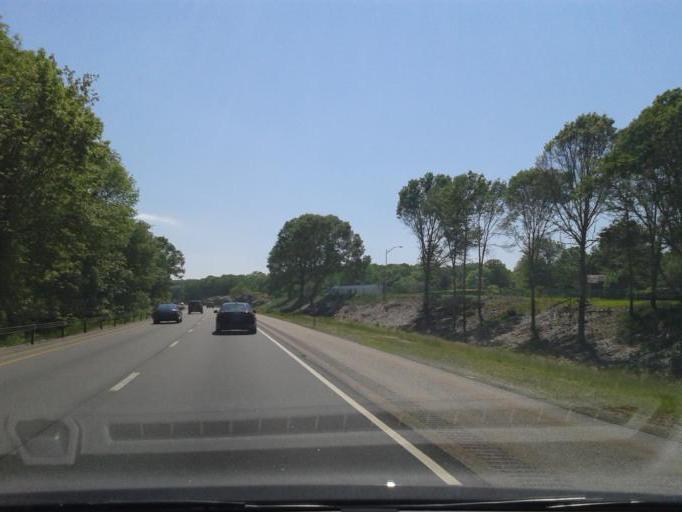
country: US
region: Connecticut
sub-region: New London County
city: Pawcatuck
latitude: 41.4174
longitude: -71.8497
